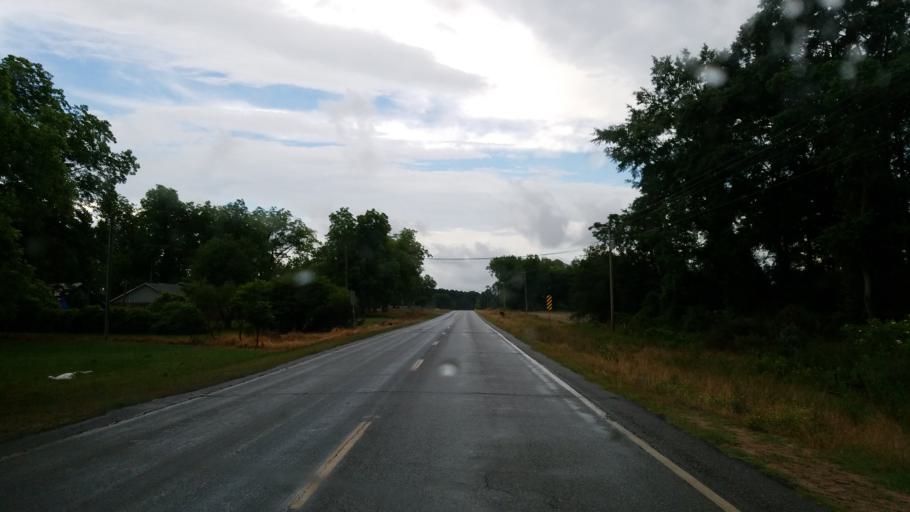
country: US
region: Georgia
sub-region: Crisp County
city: Cordele
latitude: 31.8853
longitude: -83.7674
